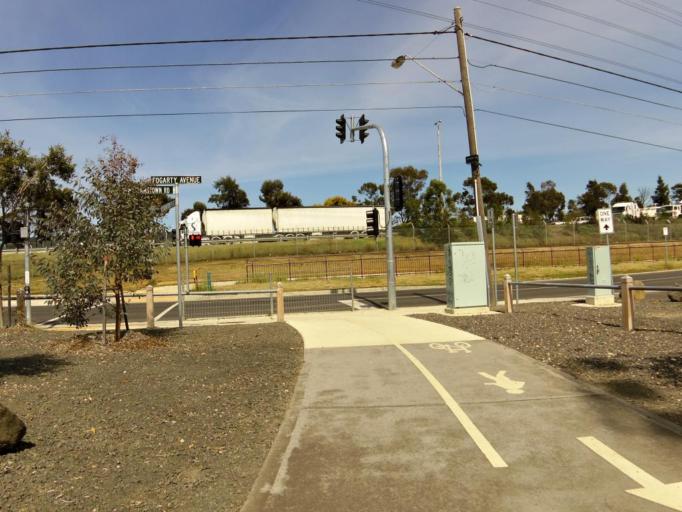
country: AU
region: Victoria
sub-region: Hobsons Bay
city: South Kingsville
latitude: -37.8237
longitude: 144.8712
